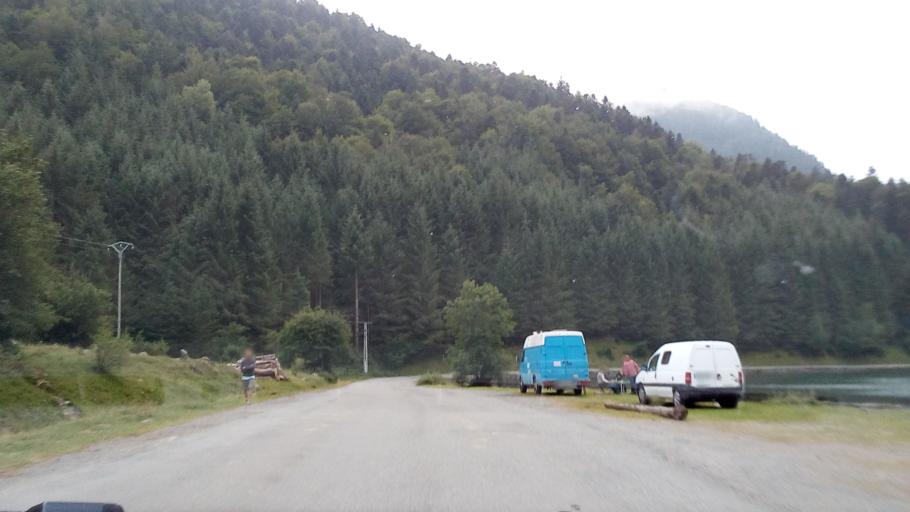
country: FR
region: Midi-Pyrenees
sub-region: Departement des Hautes-Pyrenees
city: Cauterets
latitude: 42.9077
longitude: -0.2041
